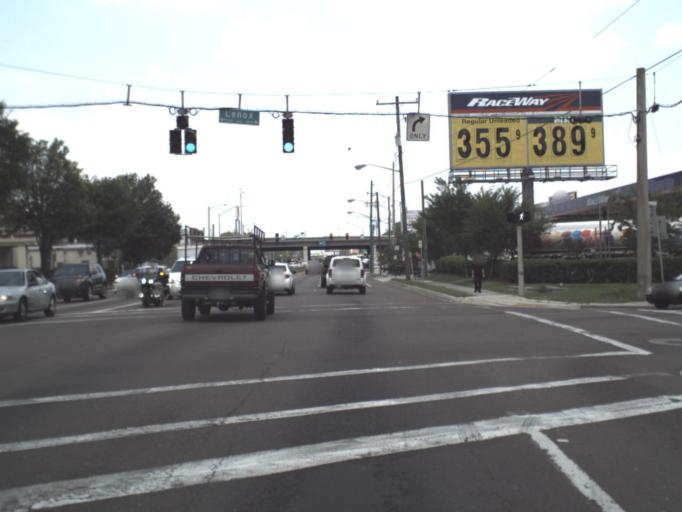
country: US
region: Florida
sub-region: Duval County
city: Jacksonville
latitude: 30.3151
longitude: -81.7306
